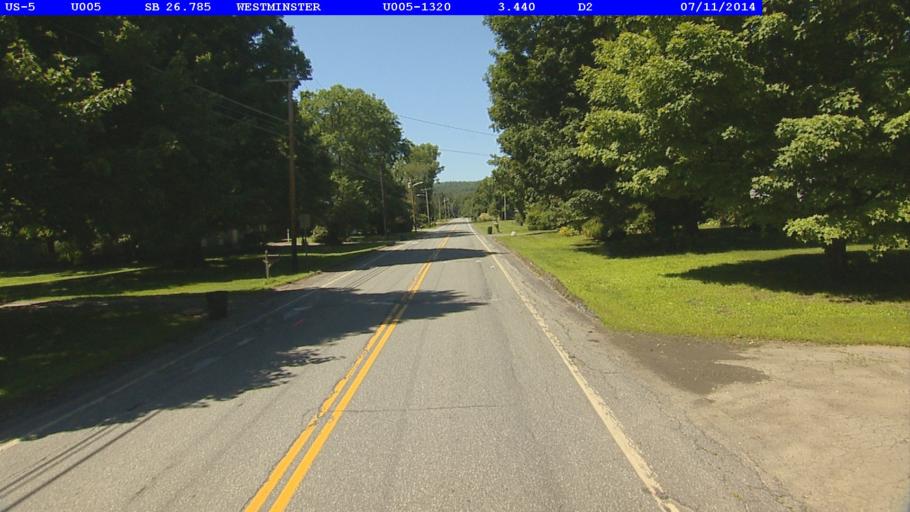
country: US
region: Vermont
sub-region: Windham County
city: Bellows Falls
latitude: 43.0663
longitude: -72.4603
